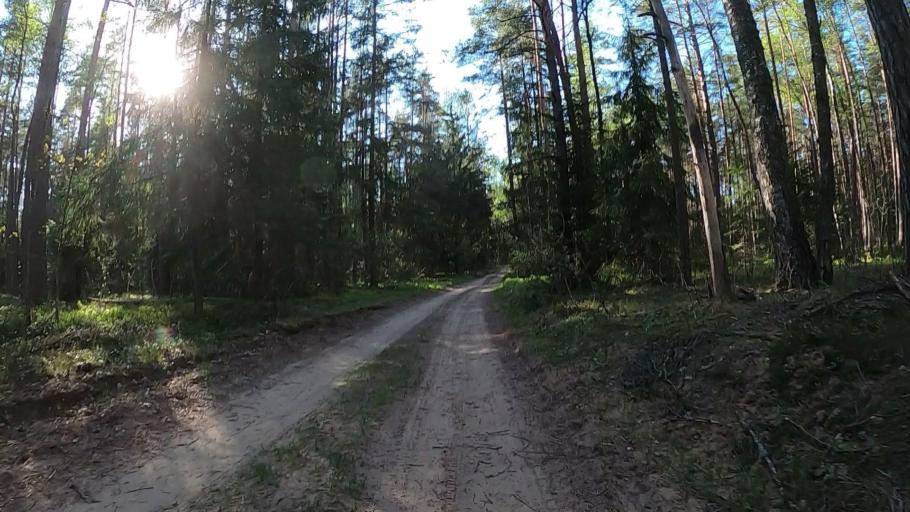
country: LV
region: Baldone
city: Baldone
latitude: 56.7663
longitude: 24.3691
